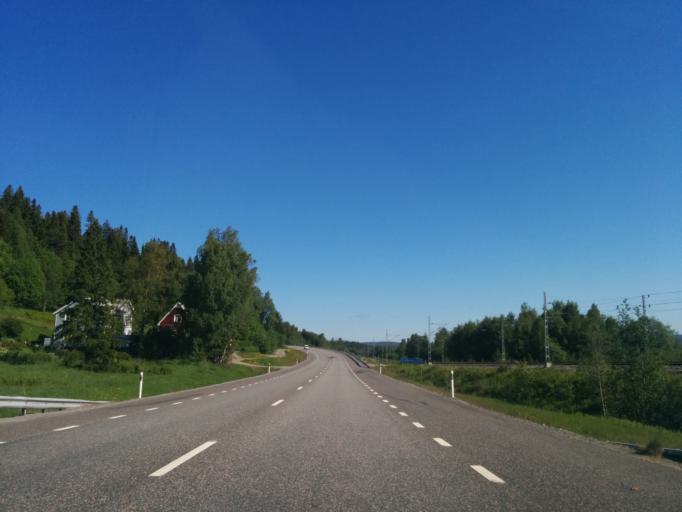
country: SE
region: Vaesternorrland
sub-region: Kramfors Kommun
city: Kramfors
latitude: 62.8585
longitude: 17.8706
